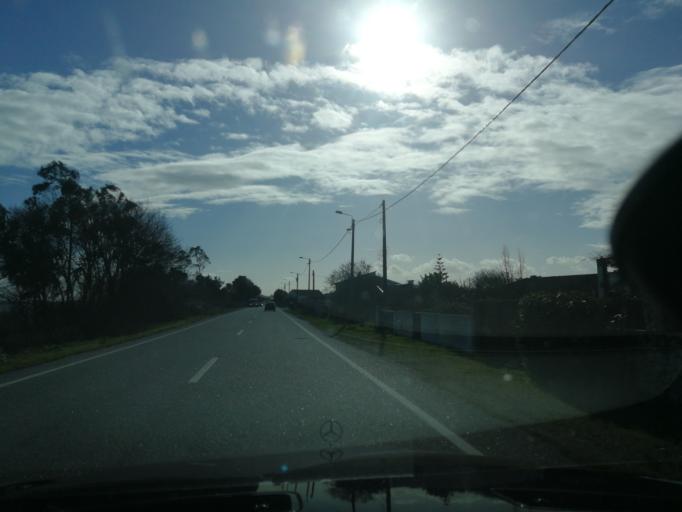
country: PT
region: Aveiro
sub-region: Estarreja
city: Pardilho
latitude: 40.8256
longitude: -8.6668
